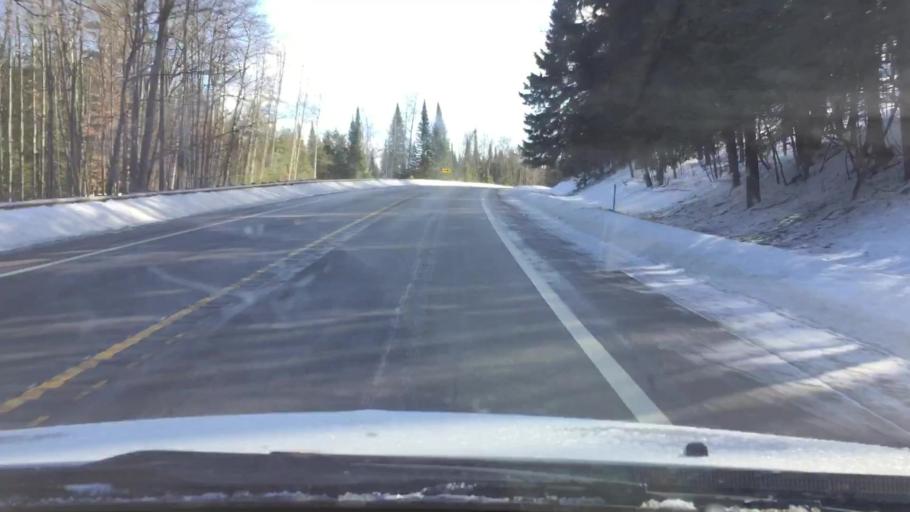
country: US
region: Michigan
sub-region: Antrim County
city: Mancelona
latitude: 44.9988
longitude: -85.0622
